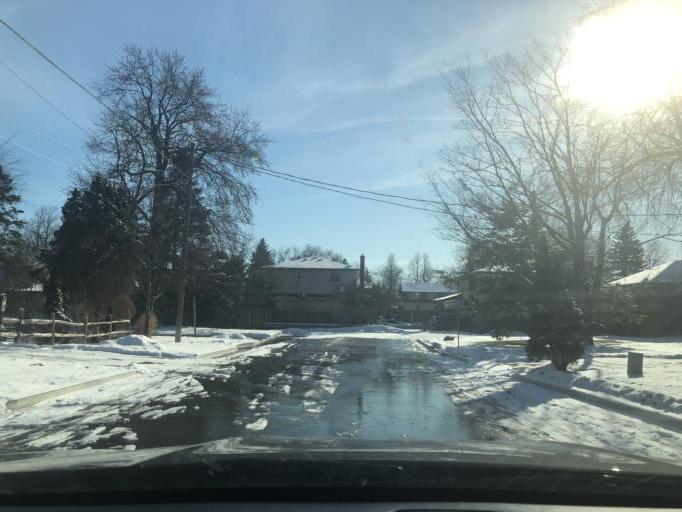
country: CA
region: Ontario
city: Scarborough
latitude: 43.7856
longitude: -79.1548
